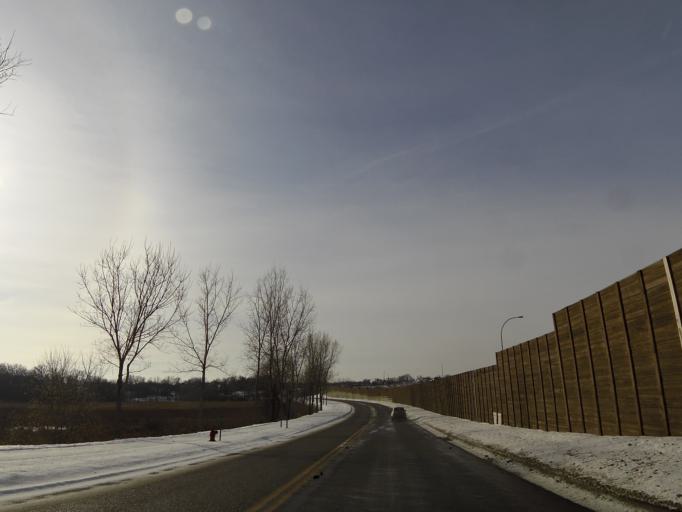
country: US
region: Minnesota
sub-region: Hennepin County
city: Eden Prairie
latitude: 44.8541
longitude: -93.4815
